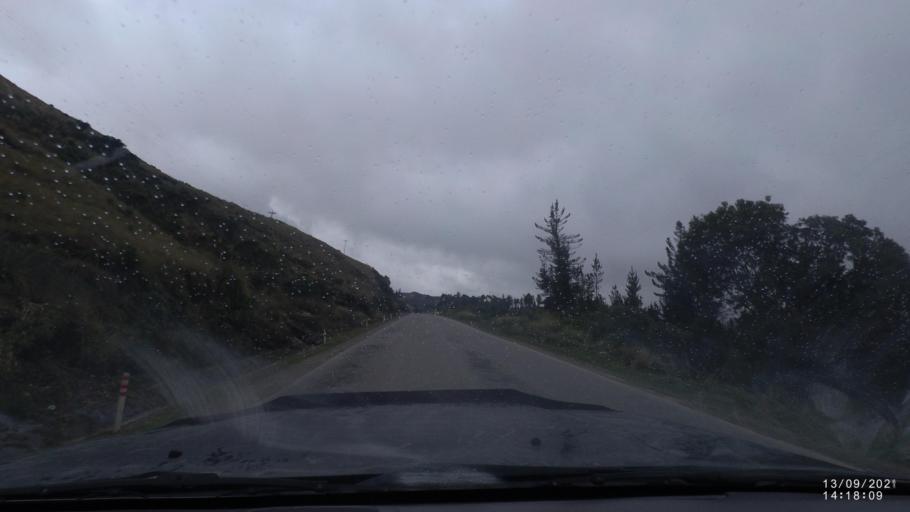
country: BO
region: Cochabamba
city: Colomi
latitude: -17.2309
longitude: -65.8874
